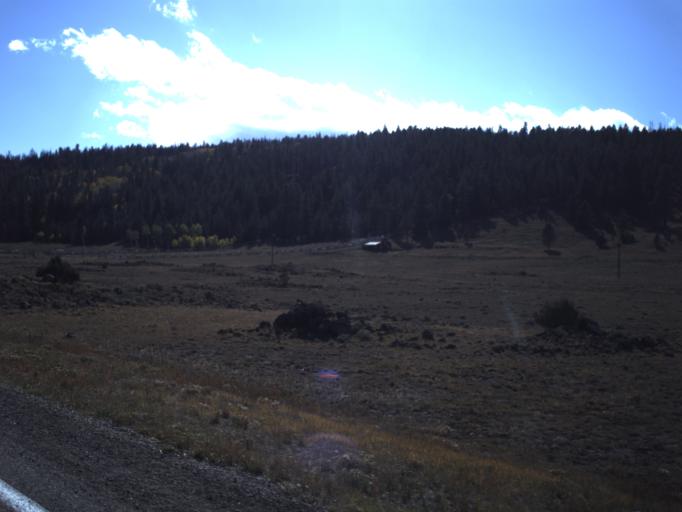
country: US
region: Utah
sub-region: Iron County
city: Parowan
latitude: 37.6767
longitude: -112.6674
